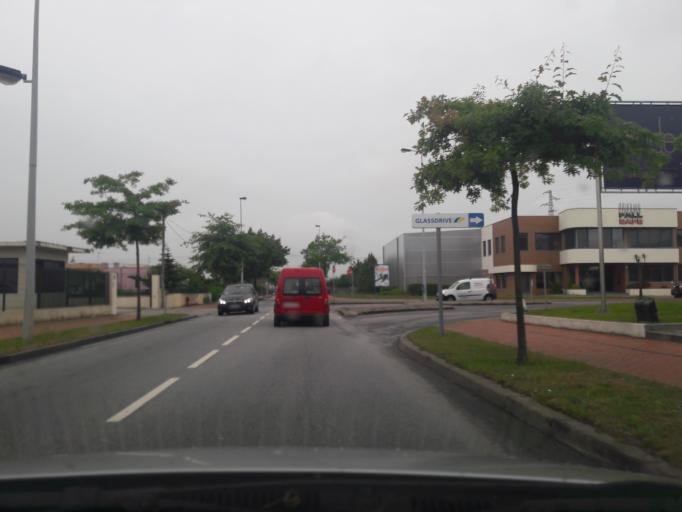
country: PT
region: Porto
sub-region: Vila do Conde
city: Arvore
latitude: 41.3308
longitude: -8.7193
